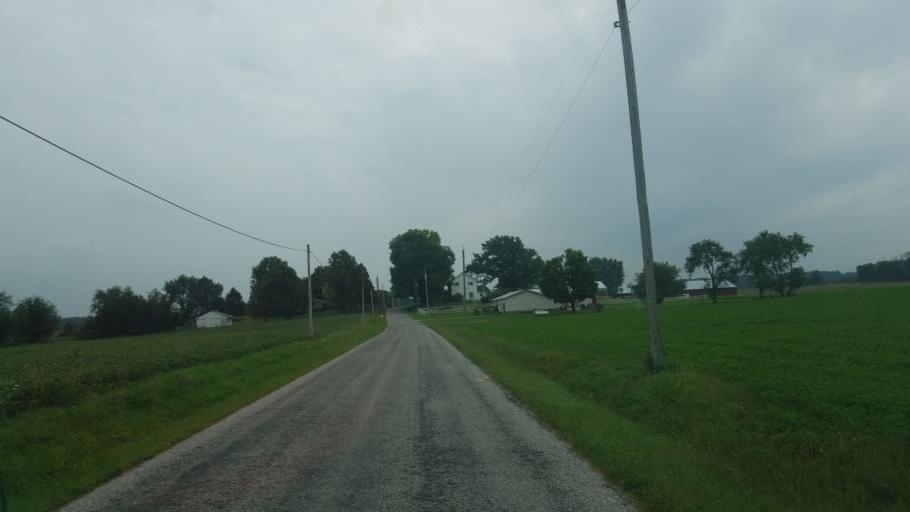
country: US
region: Ohio
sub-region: Wayne County
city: Creston
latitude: 40.9567
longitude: -81.8506
